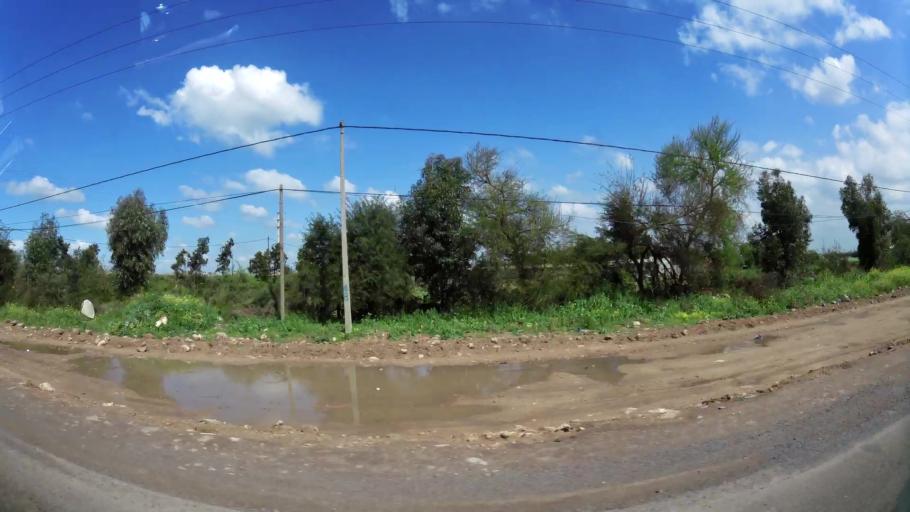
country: MA
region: Grand Casablanca
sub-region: Mediouna
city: Mediouna
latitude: 33.4386
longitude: -7.5206
